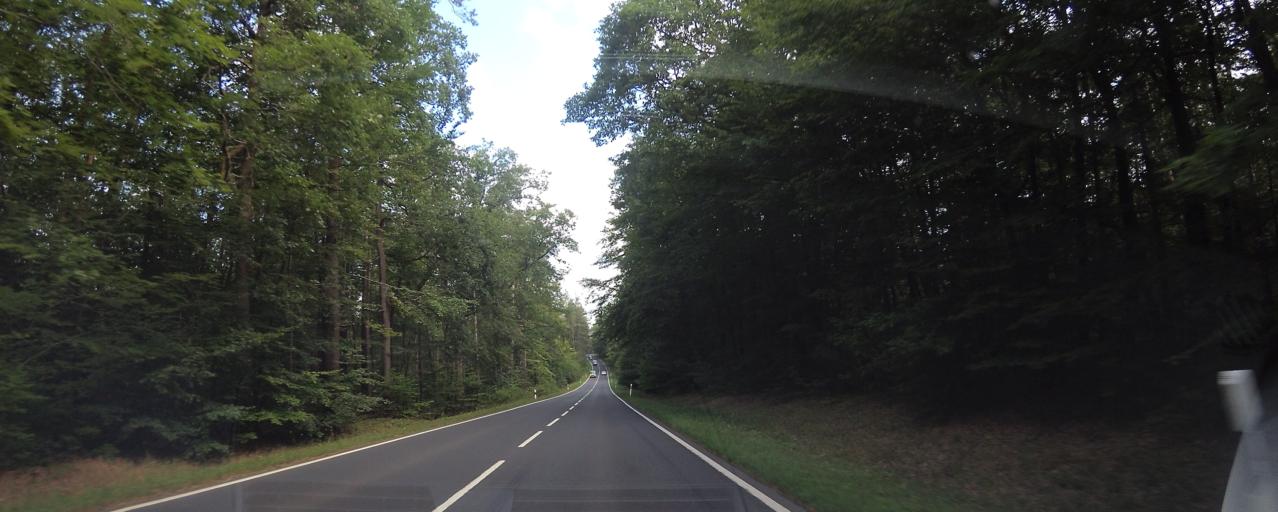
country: DE
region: Rheinland-Pfalz
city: Zemmer
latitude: 49.9105
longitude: 6.7071
